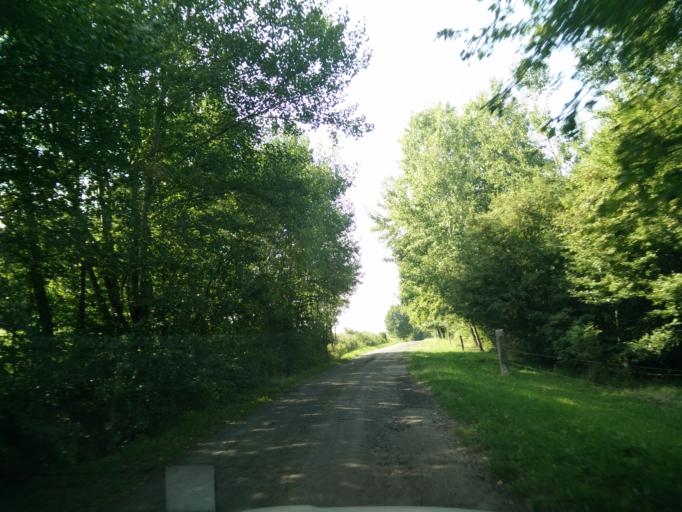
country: SK
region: Nitriansky
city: Novaky
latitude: 48.6782
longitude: 18.6175
